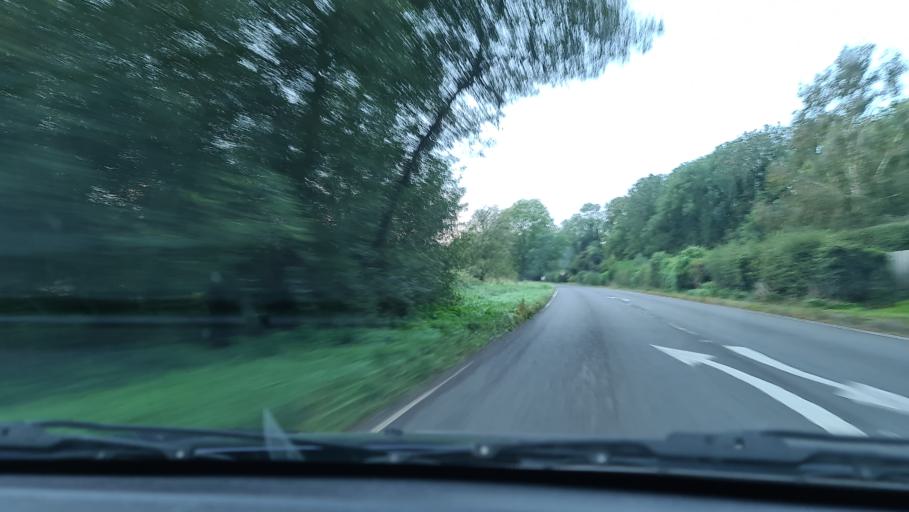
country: GB
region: England
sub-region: Hampshire
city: Kings Worthy
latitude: 51.1605
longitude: -1.3375
